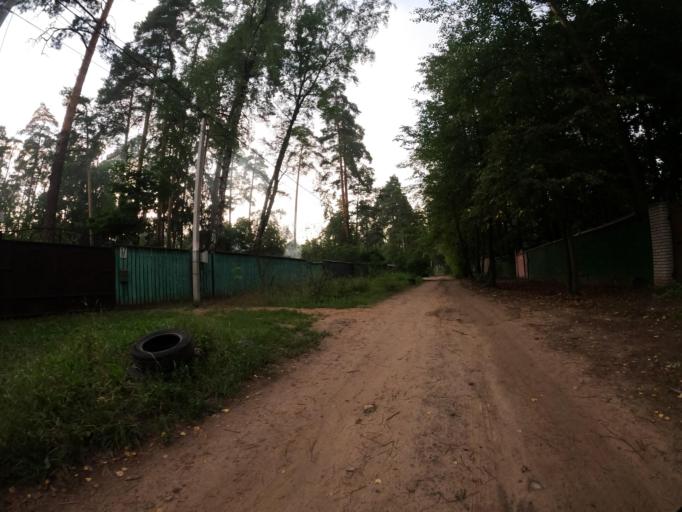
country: RU
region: Moskovskaya
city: Rodniki
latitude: 55.6402
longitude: 38.0652
